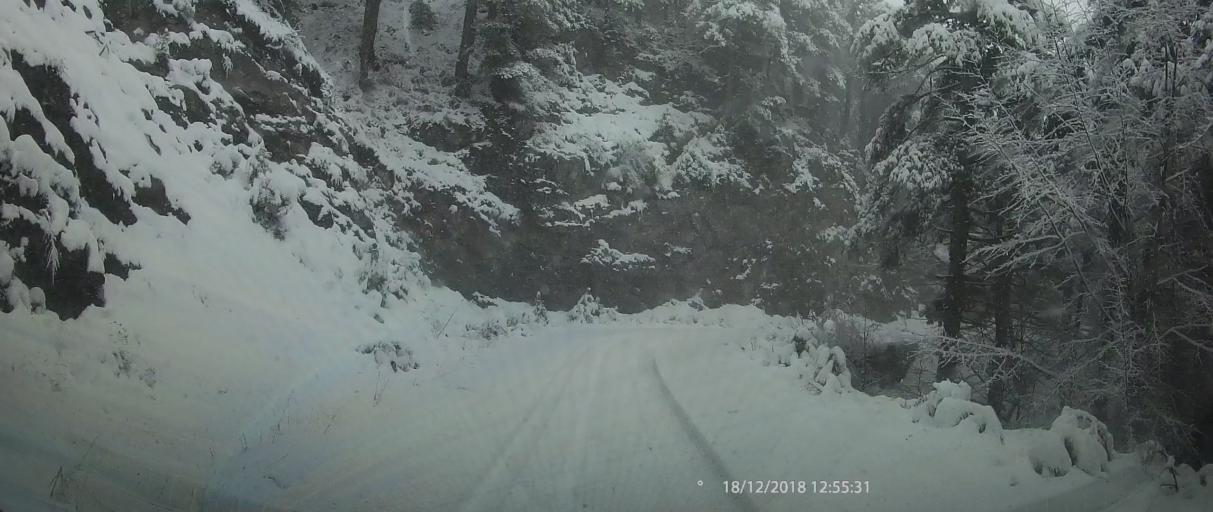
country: GR
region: Central Macedonia
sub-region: Nomos Pierias
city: Litochoro
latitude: 40.1057
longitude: 22.4574
